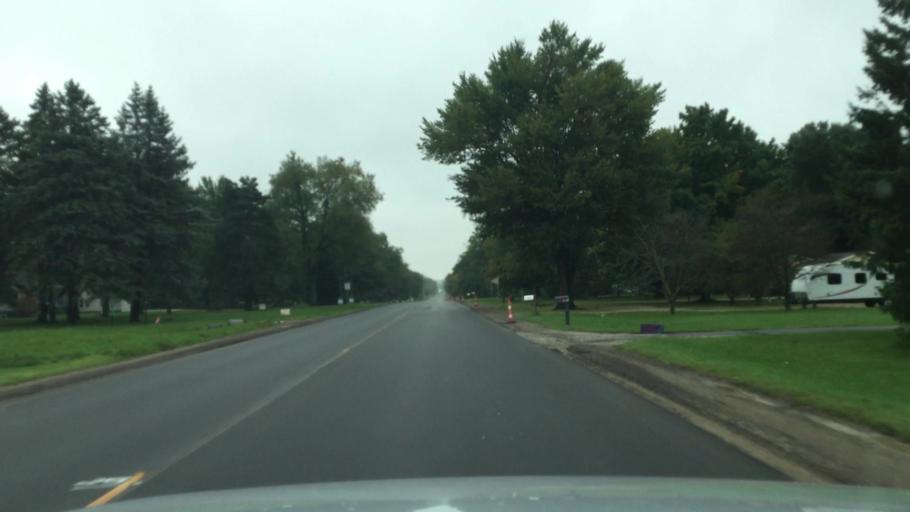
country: US
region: Michigan
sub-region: Shiawassee County
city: Perry
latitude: 42.8898
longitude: -84.2219
